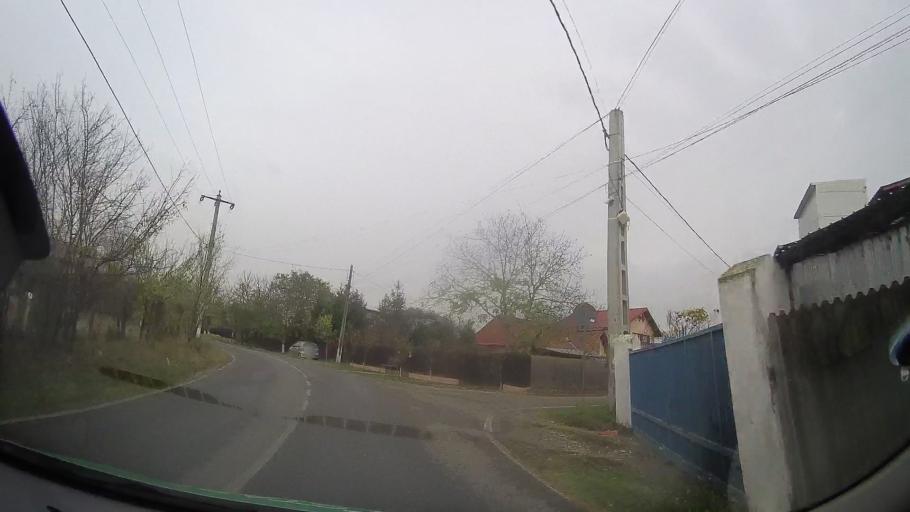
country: RO
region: Ilfov
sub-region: Comuna Gruiu
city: Gruiu
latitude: 44.7239
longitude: 26.2136
